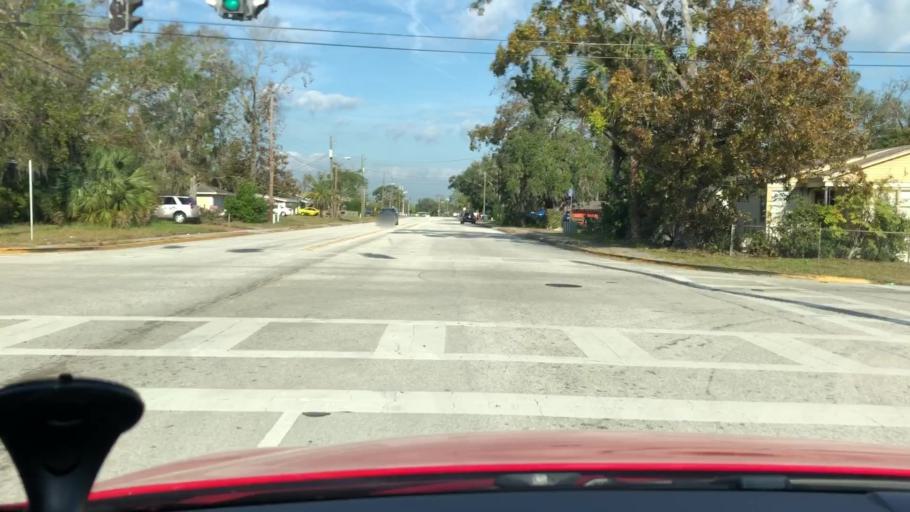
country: US
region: Florida
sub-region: Volusia County
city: Daytona Beach
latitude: 29.2142
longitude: -81.0526
